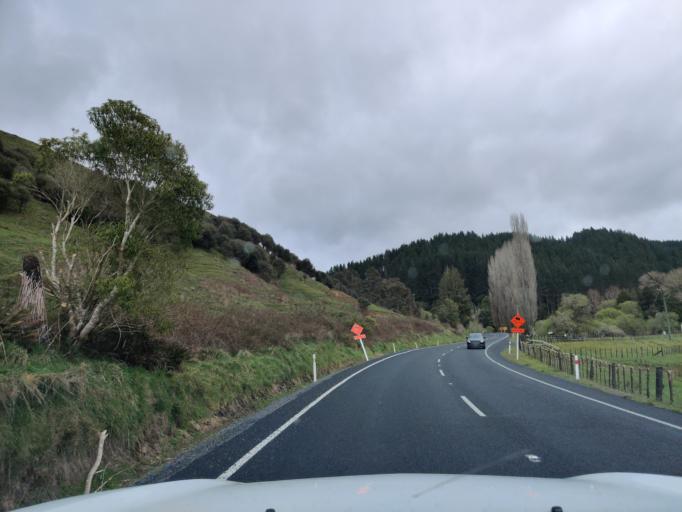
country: NZ
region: Waikato
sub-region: Otorohanga District
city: Otorohanga
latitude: -38.6495
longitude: 175.2110
